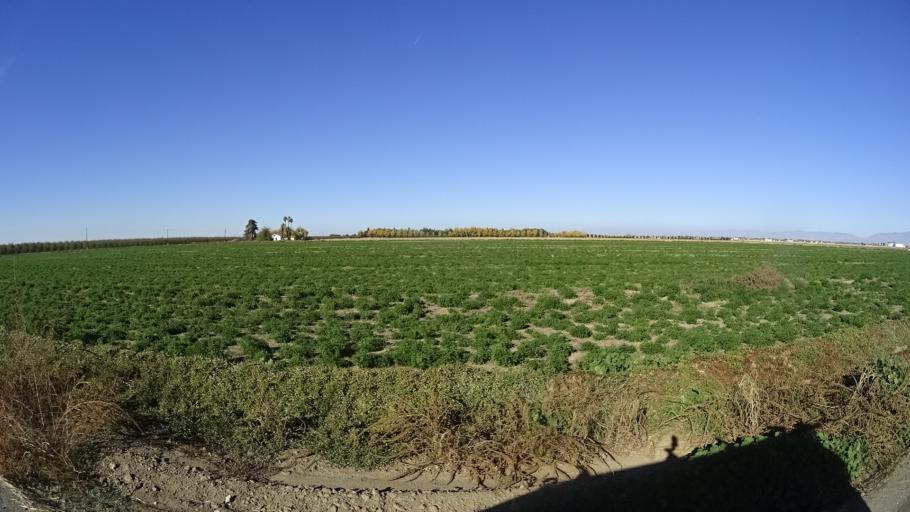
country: US
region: California
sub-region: Kern County
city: Greenacres
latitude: 35.2813
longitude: -119.1263
